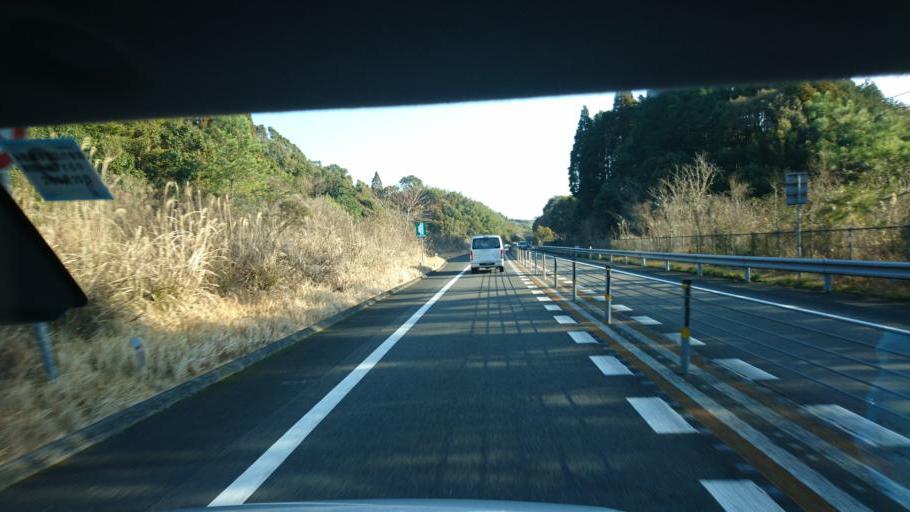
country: JP
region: Miyazaki
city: Tsuma
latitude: 32.0123
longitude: 131.3814
